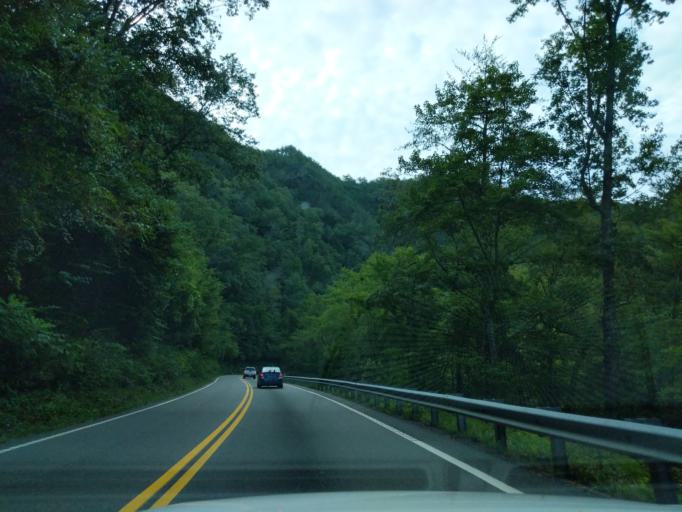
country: US
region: Georgia
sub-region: Fannin County
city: McCaysville
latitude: 35.0808
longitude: -84.5082
